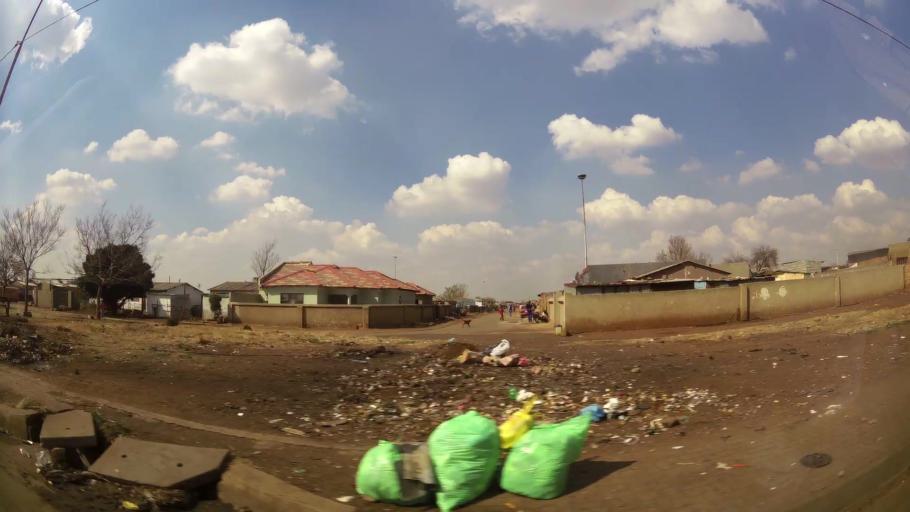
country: ZA
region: Gauteng
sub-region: Ekurhuleni Metropolitan Municipality
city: Germiston
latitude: -26.3060
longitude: 28.1491
